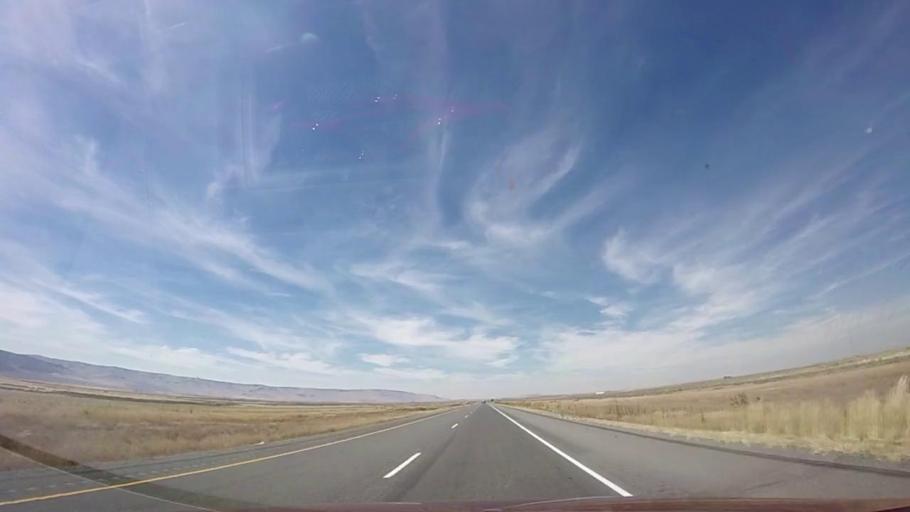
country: US
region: Idaho
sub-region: Minidoka County
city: Rupert
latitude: 42.3965
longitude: -113.2970
